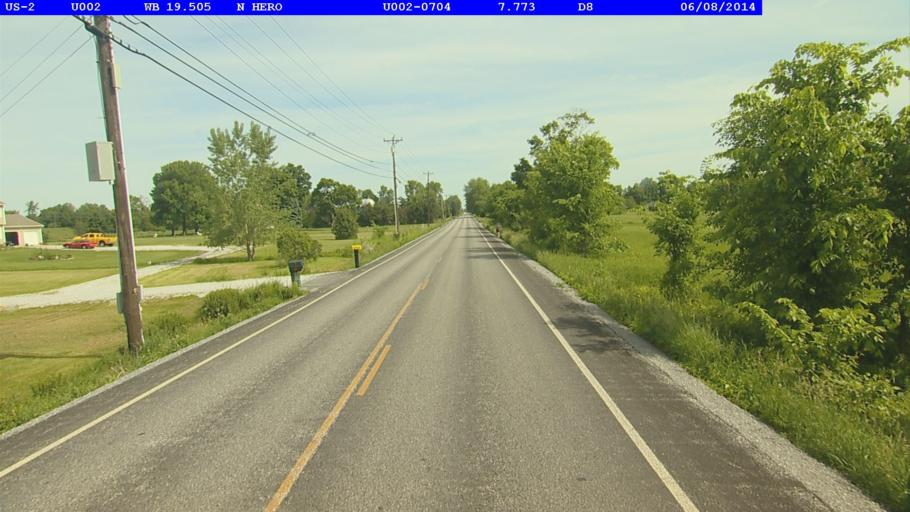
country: US
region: Vermont
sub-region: Grand Isle County
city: North Hero
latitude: 44.7878
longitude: -73.2930
